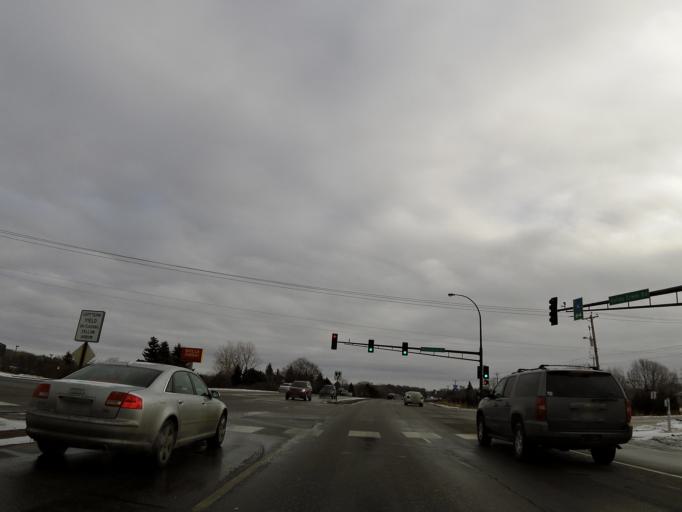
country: US
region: Minnesota
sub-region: Washington County
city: Woodbury
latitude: 44.9239
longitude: -92.9548
